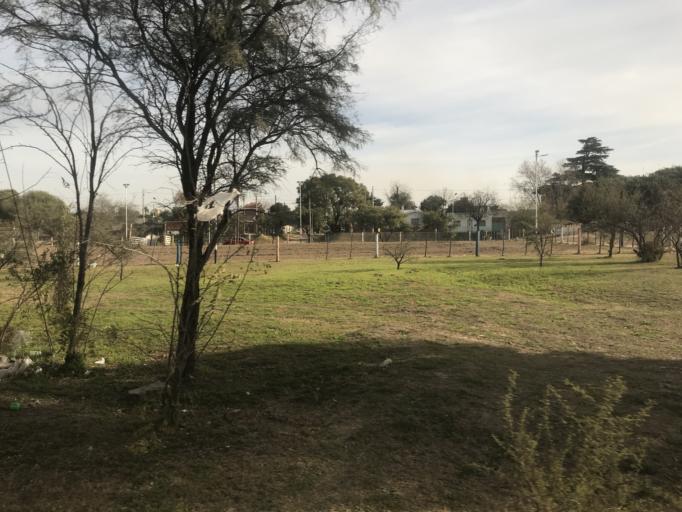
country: AR
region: Cordoba
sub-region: Departamento de Rio Segundo
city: Rio Segundo
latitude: -31.6546
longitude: -63.9096
